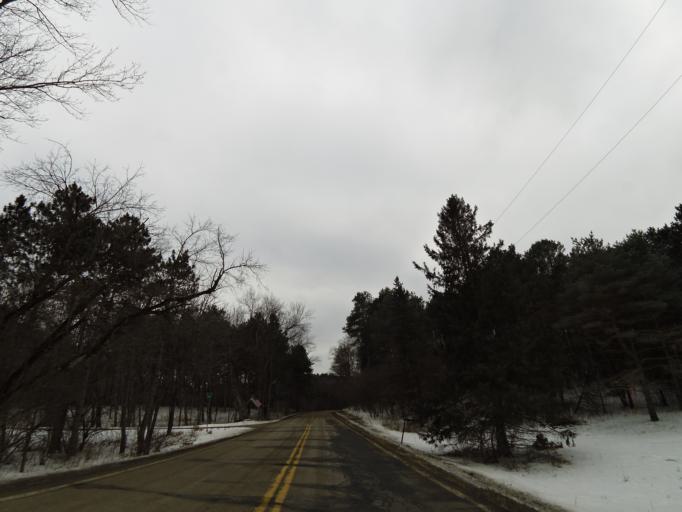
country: US
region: Minnesota
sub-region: Washington County
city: Lake Saint Croix Beach
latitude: 44.9338
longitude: -92.7977
